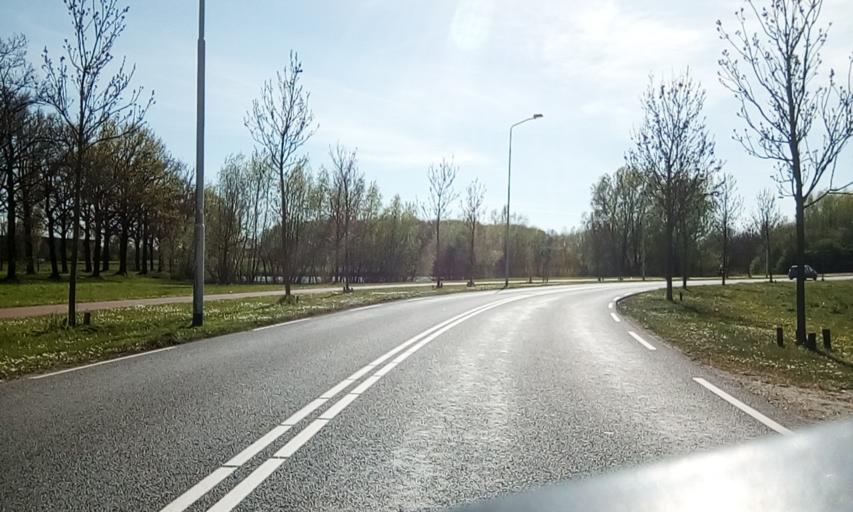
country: NL
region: Gelderland
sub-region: Gemeente Wijchen
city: Wijchen
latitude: 51.8288
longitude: 5.7411
